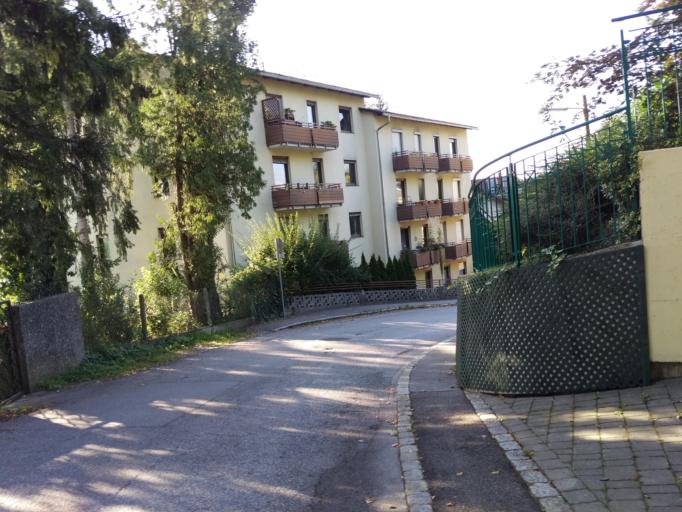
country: AT
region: Styria
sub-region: Graz Stadt
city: Graz
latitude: 47.0729
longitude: 15.4609
